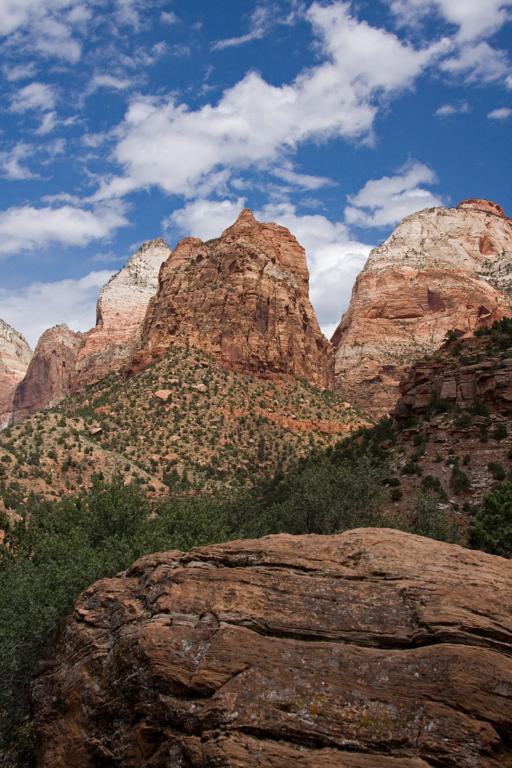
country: US
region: Utah
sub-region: Washington County
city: Hildale
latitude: 37.2104
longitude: -112.9794
